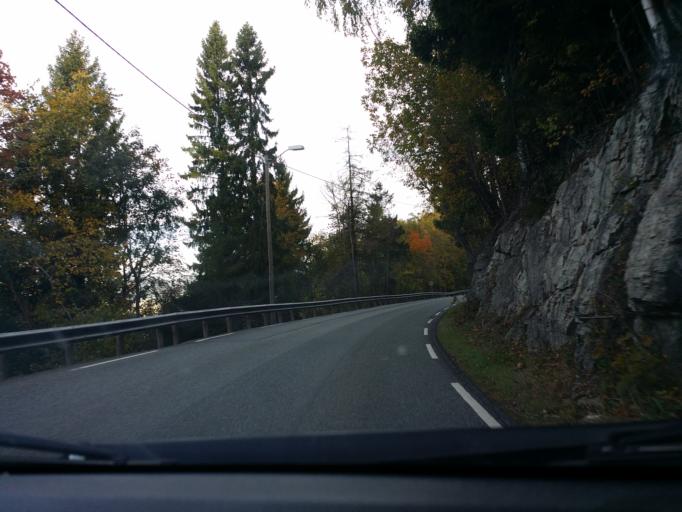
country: NO
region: Buskerud
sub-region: Lier
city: Tranby
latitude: 59.8418
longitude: 10.2667
